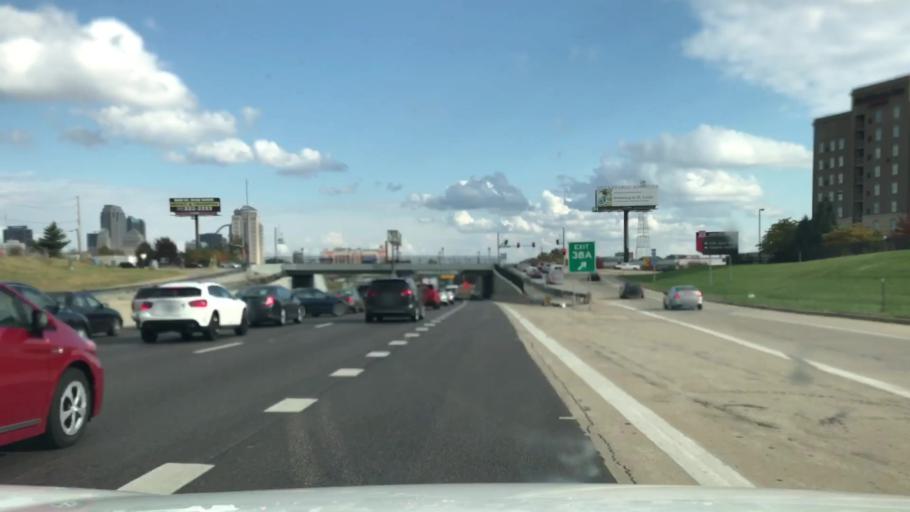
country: US
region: Missouri
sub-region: City of Saint Louis
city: St. Louis
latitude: 38.6280
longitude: -90.2198
